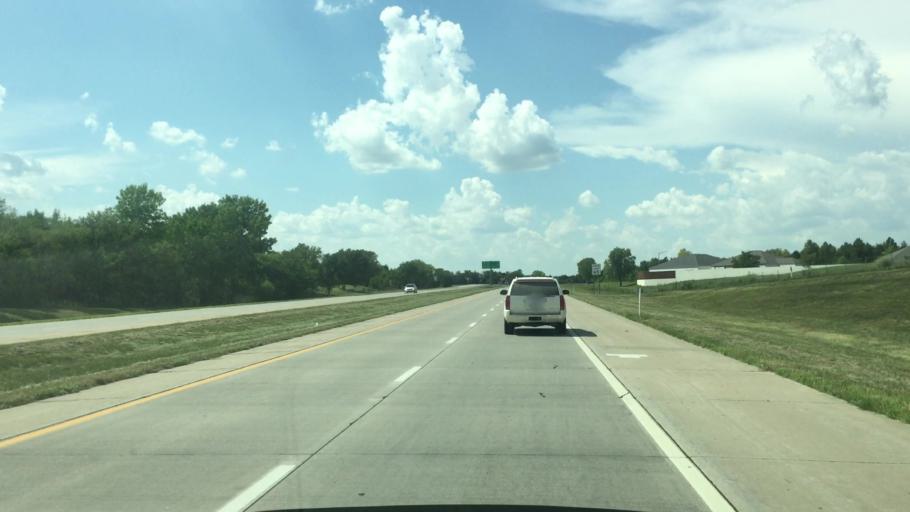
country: US
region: Kansas
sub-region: Butler County
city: Andover
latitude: 37.6975
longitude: -97.1919
